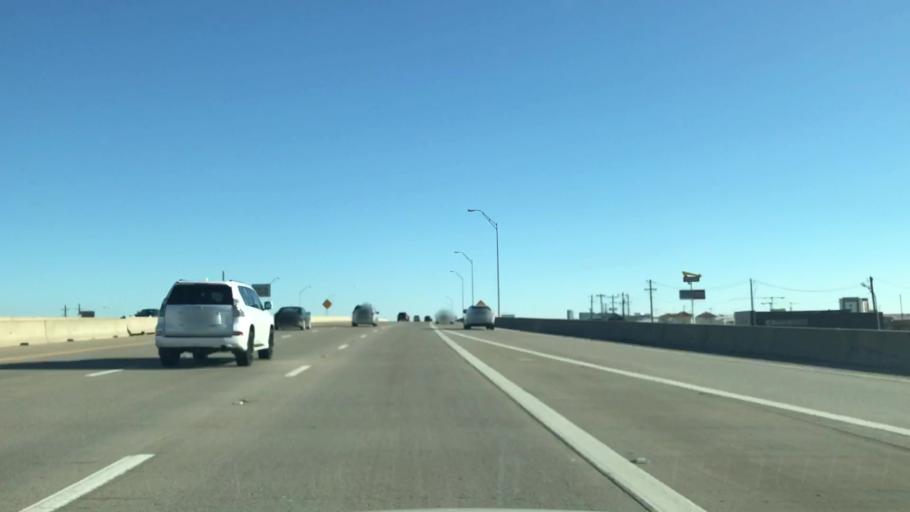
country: US
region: Texas
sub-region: Denton County
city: The Colony
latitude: 33.0703
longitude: -96.8788
